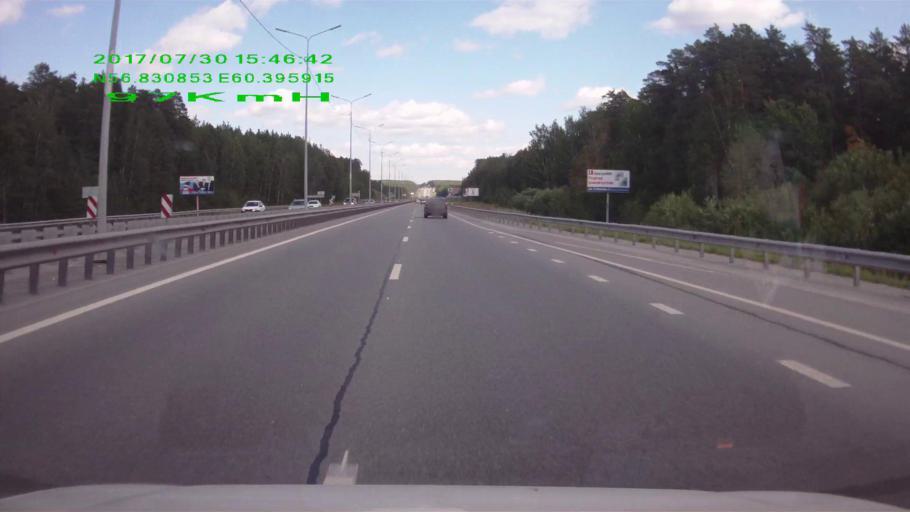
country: RU
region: Sverdlovsk
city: Shirokaya Rechka
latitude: 56.8308
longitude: 60.3964
